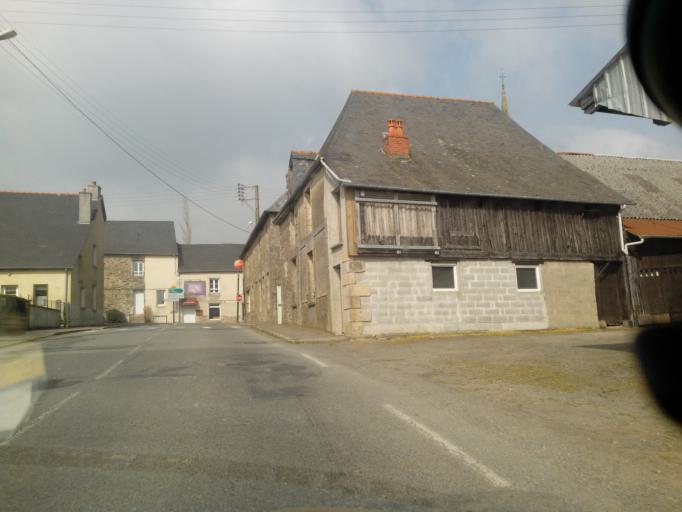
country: FR
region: Brittany
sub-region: Departement des Cotes-d'Armor
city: Caulnes
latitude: 48.2666
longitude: -2.1599
